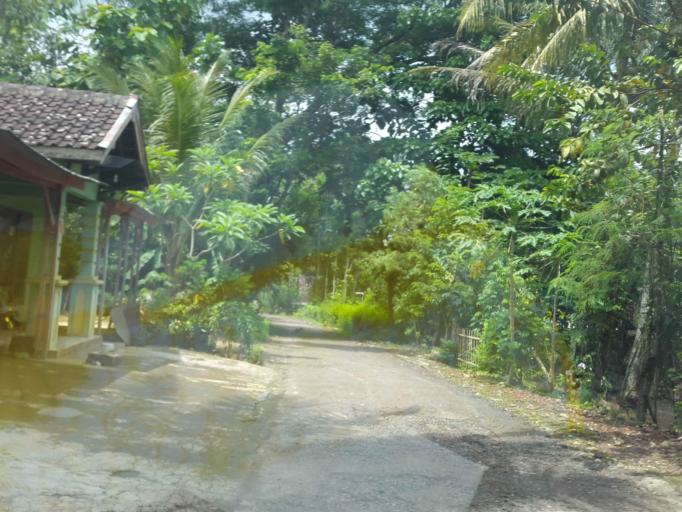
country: ID
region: Daerah Istimewa Yogyakarta
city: Wonosari
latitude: -7.9359
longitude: 110.6245
